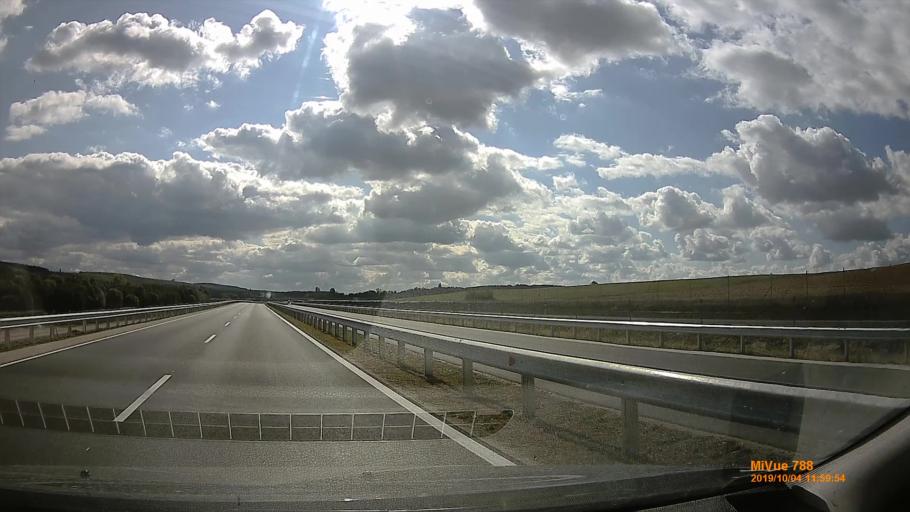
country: HU
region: Somogy
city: Karad
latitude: 46.6320
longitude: 17.7917
